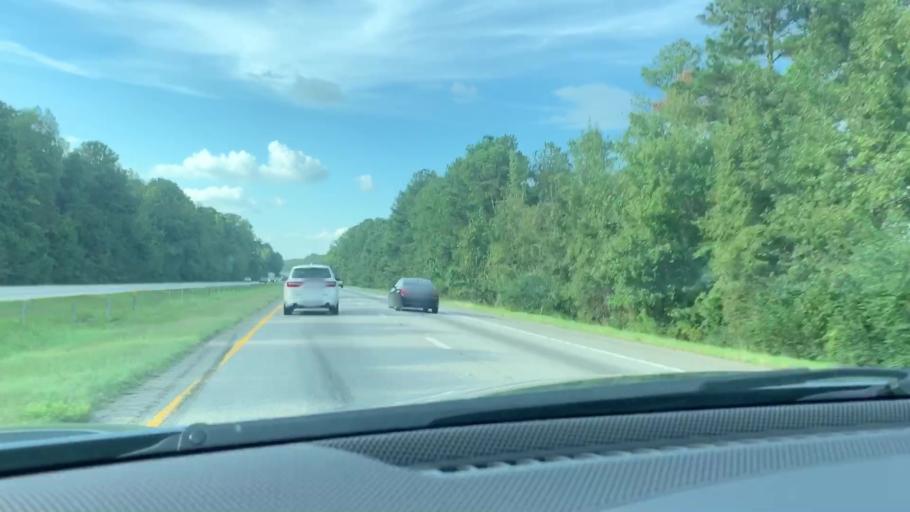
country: US
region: South Carolina
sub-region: Orangeburg County
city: Brookdale
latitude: 33.4897
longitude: -80.7622
